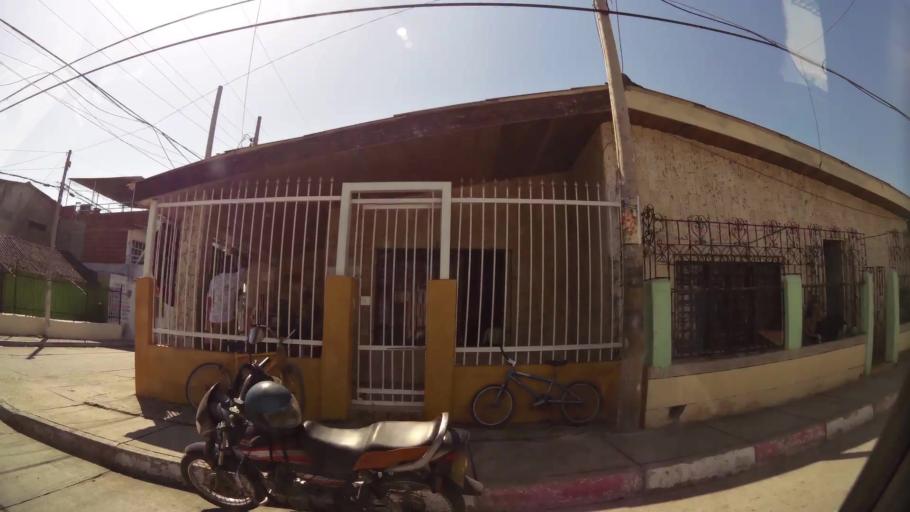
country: CO
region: Bolivar
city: Cartagena
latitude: 10.4412
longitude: -75.5181
